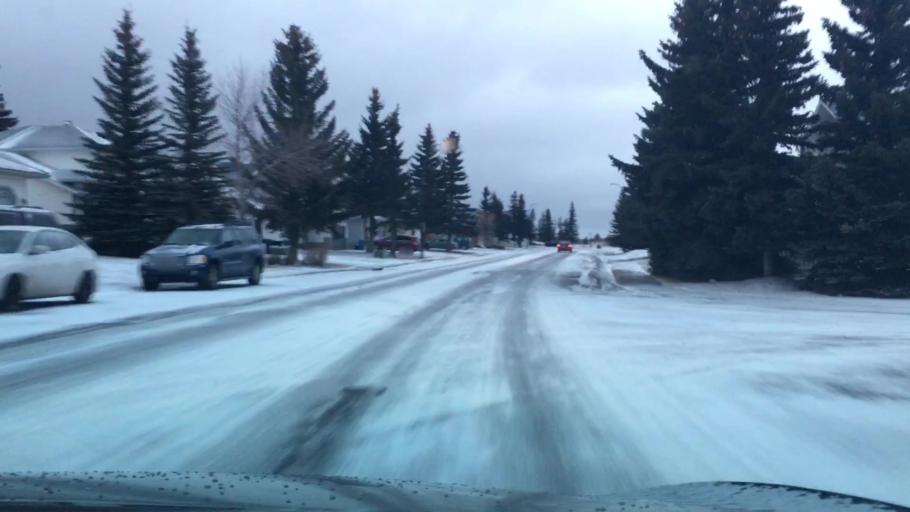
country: CA
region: Alberta
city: Calgary
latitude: 51.1343
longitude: -114.1674
